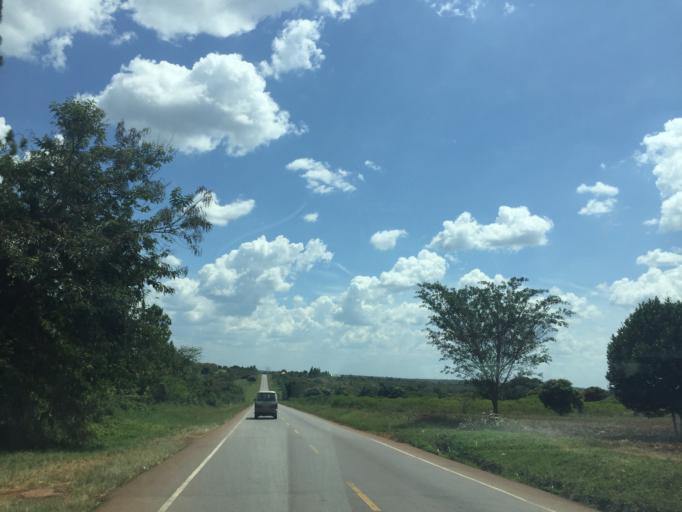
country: UG
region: Central Region
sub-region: Nakasongola District
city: Nakasongola
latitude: 1.3192
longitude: 32.4221
